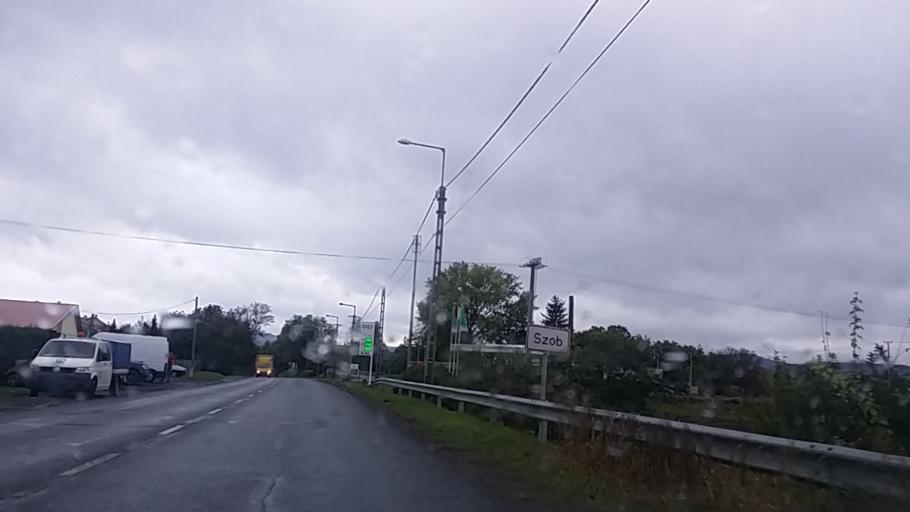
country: HU
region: Pest
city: Szob
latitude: 47.8152
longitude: 18.8830
